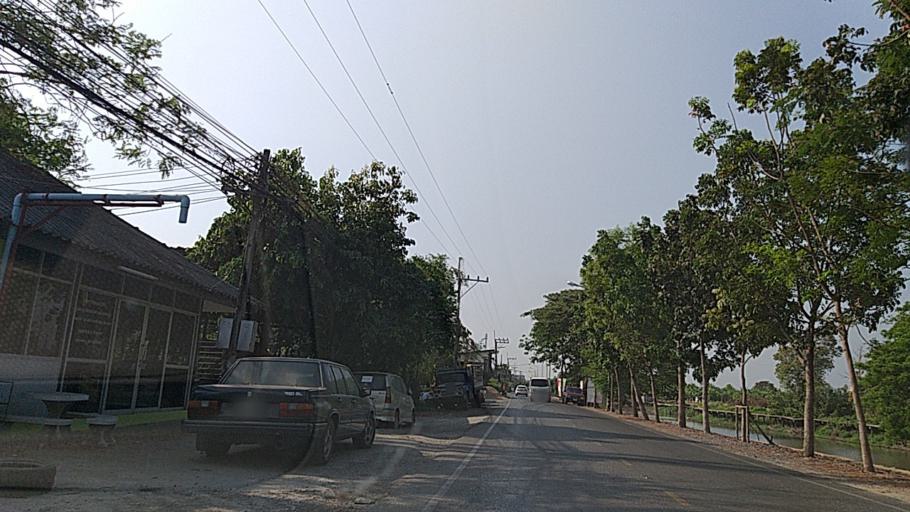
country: TH
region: Pathum Thani
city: Lam Luk Ka
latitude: 13.9438
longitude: 100.7060
